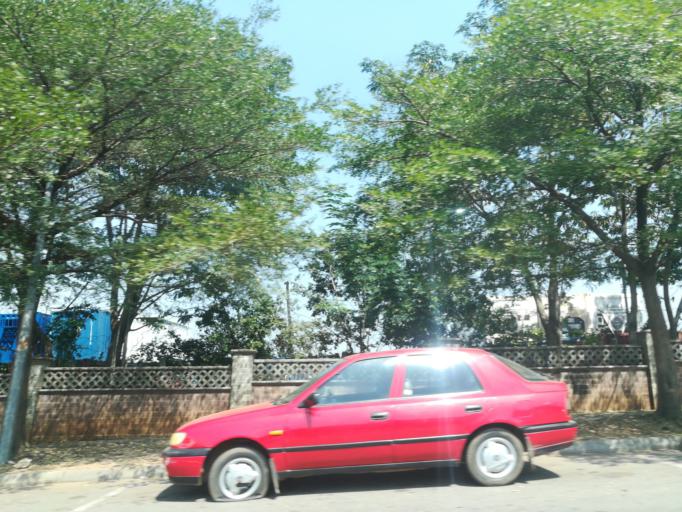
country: NG
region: Abuja Federal Capital Territory
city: Abuja
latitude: 9.0645
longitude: 7.4505
